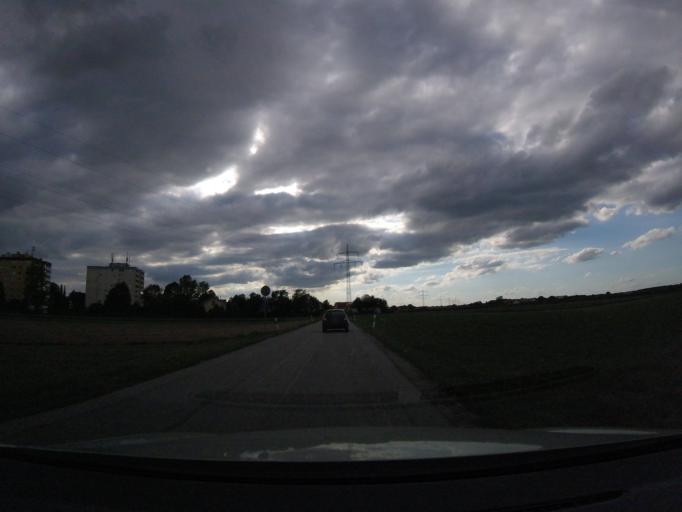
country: DE
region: Bavaria
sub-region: Upper Bavaria
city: Putzbrunn
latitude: 48.0791
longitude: 11.7255
